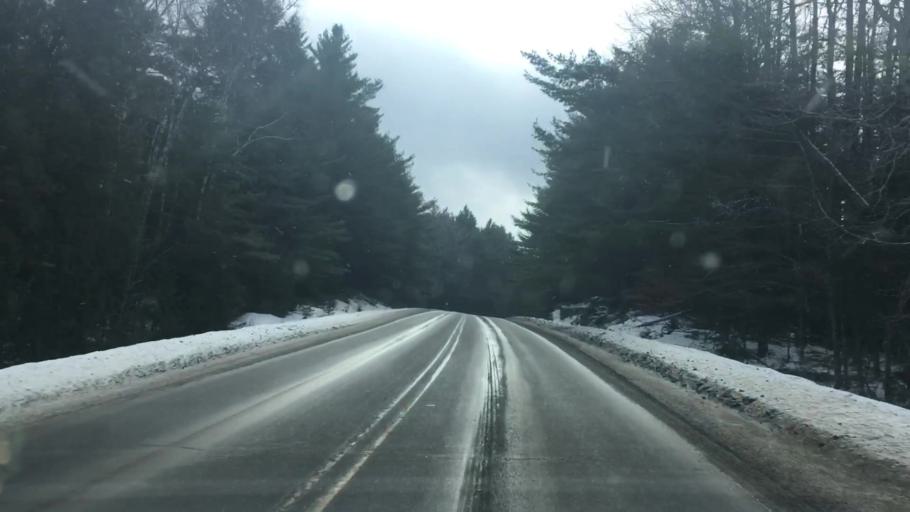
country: US
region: Maine
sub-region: Washington County
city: Calais
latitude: 45.0448
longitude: -67.3277
